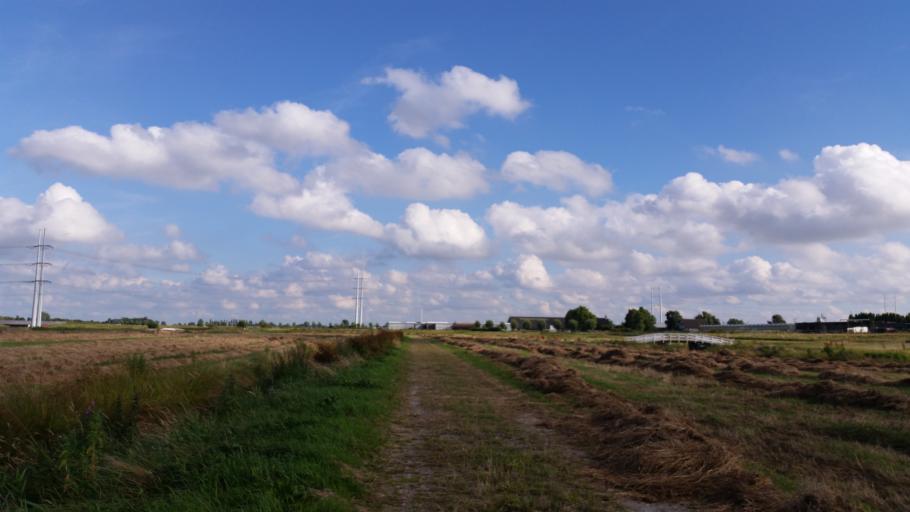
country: NL
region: South Holland
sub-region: Gemeente Zoetermeer
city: Zoetermeer
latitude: 52.0323
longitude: 4.4655
